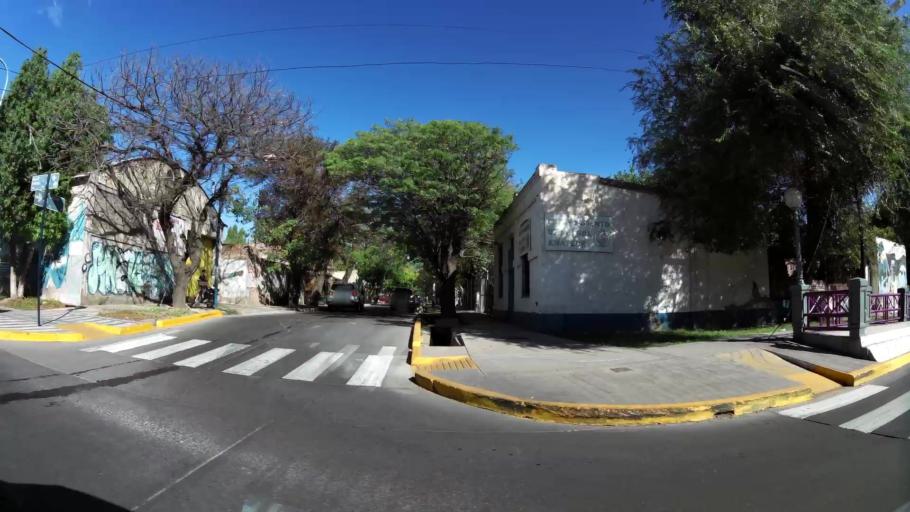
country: AR
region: Mendoza
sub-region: Departamento de Godoy Cruz
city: Godoy Cruz
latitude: -32.9210
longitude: -68.8415
